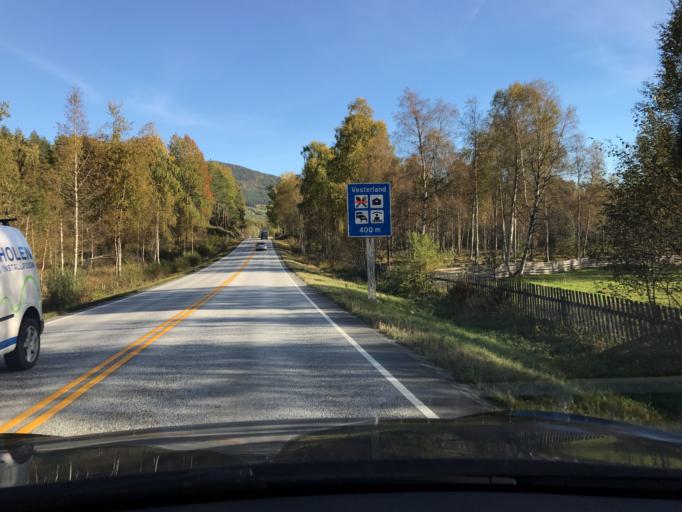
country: NO
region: Sogn og Fjordane
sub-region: Sogndal
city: Sogndalsfjora
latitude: 61.2069
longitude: 7.1914
